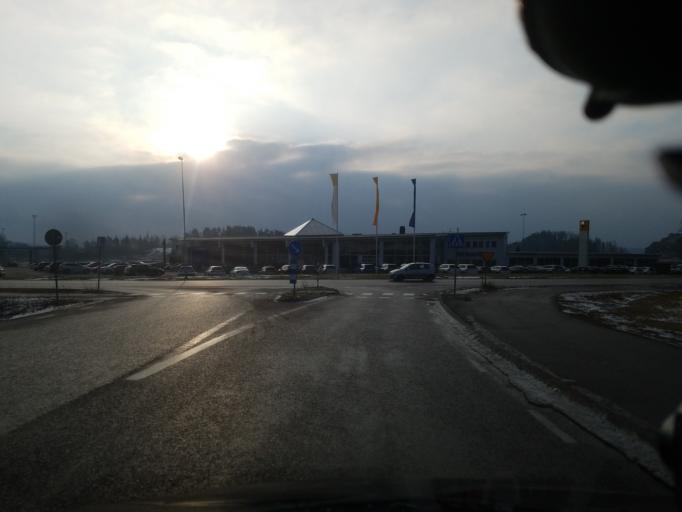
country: SE
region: Vaestra Goetaland
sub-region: Uddevalla Kommun
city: Uddevalla
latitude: 58.3506
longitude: 11.8682
